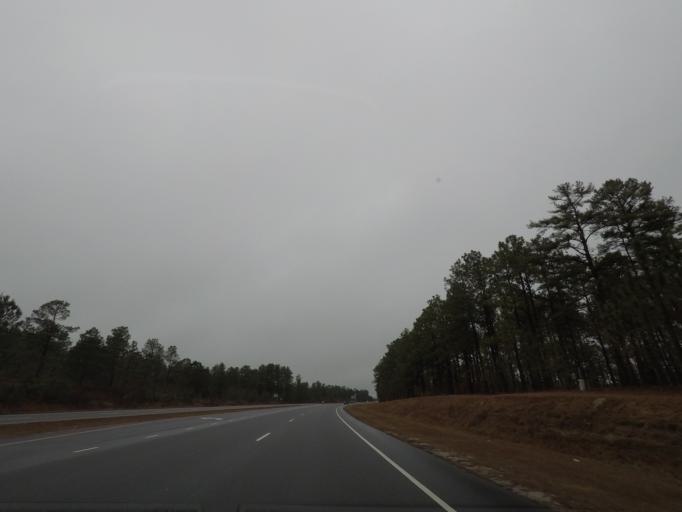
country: US
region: North Carolina
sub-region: Cumberland County
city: Spring Lake
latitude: 35.2344
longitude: -79.0192
